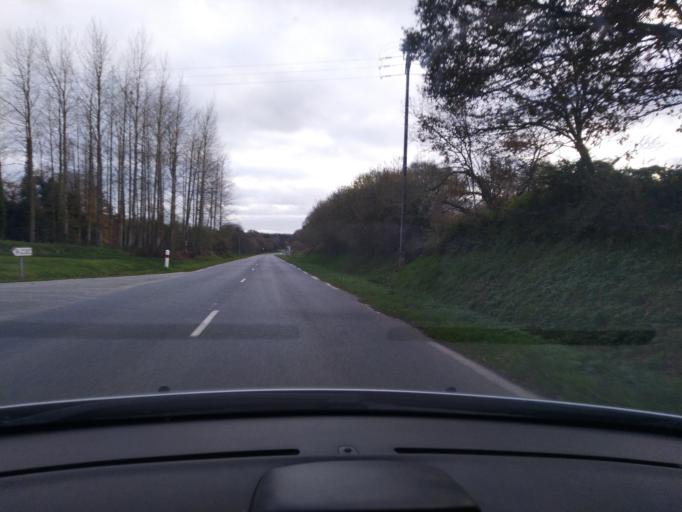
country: FR
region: Brittany
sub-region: Departement des Cotes-d'Armor
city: Plouaret
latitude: 48.5851
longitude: -3.4948
